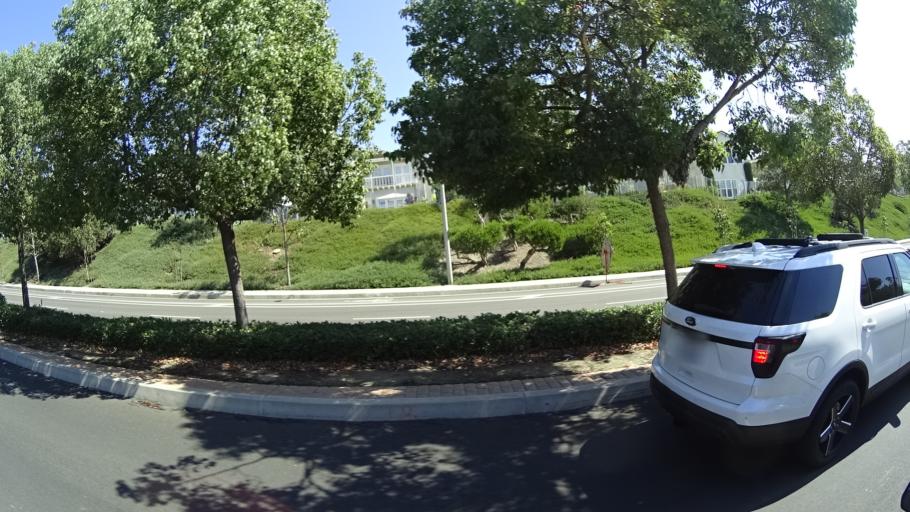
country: US
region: California
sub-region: Orange County
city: San Clemente
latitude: 33.4594
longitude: -117.6186
